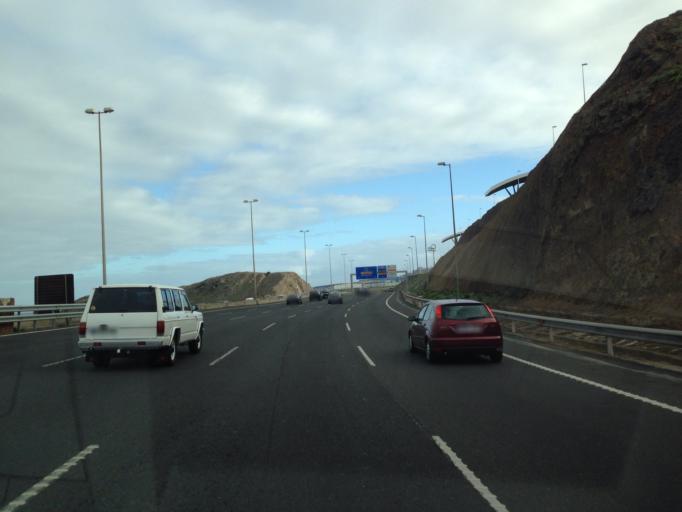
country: ES
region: Canary Islands
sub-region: Provincia de Las Palmas
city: Telde
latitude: 28.0359
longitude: -15.4053
